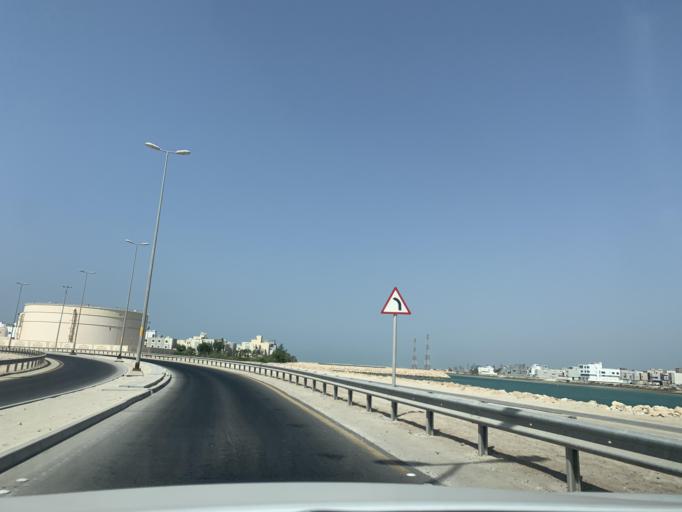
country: BH
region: Manama
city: Jidd Hafs
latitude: 26.2316
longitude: 50.4615
